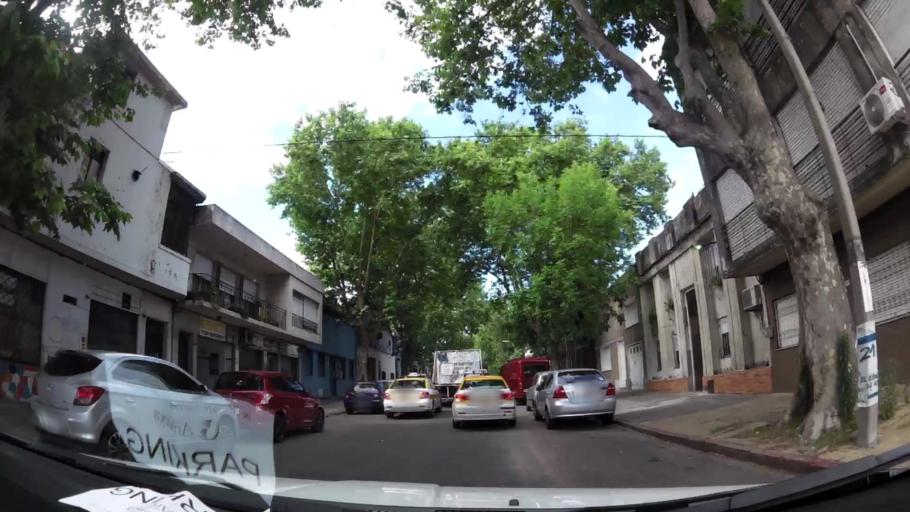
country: UY
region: Montevideo
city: Montevideo
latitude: -34.8822
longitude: -56.1836
